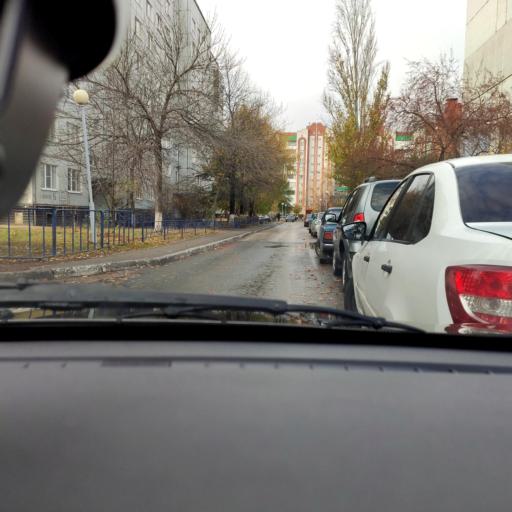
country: RU
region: Samara
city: Tol'yatti
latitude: 53.5380
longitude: 49.3278
